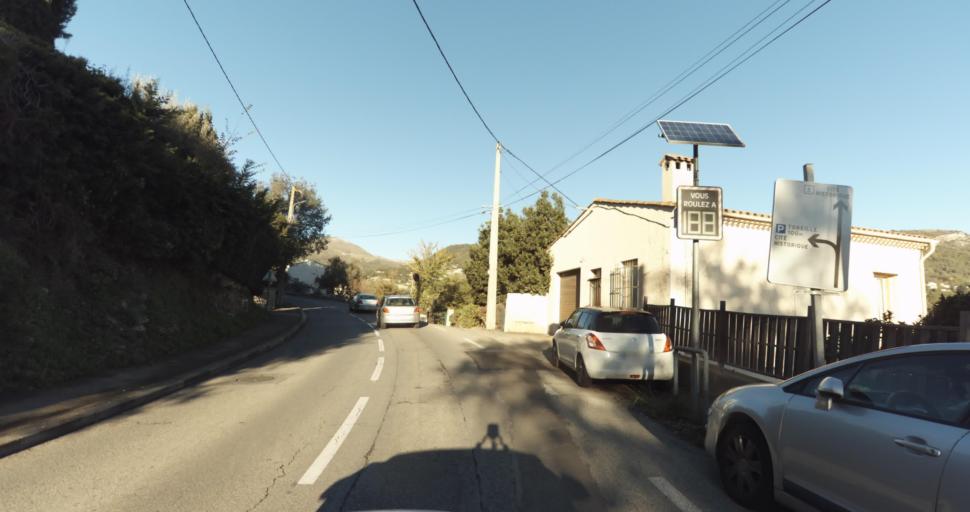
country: FR
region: Provence-Alpes-Cote d'Azur
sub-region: Departement des Alpes-Maritimes
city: Vence
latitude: 43.7224
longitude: 7.1186
